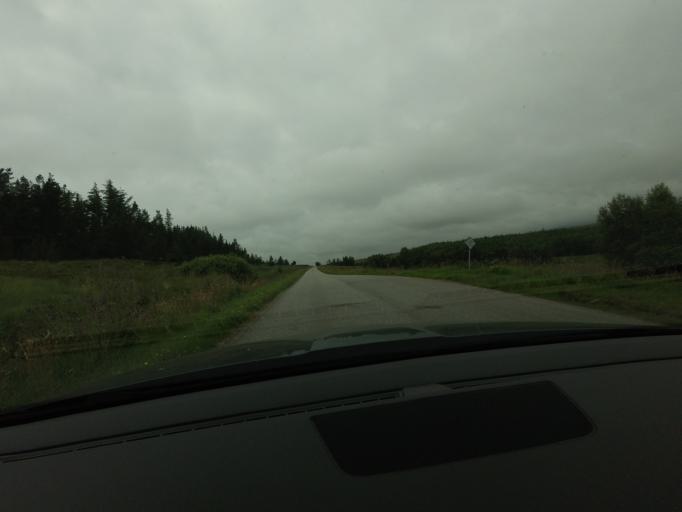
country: GB
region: Scotland
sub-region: Highland
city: Alness
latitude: 58.1298
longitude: -4.4586
